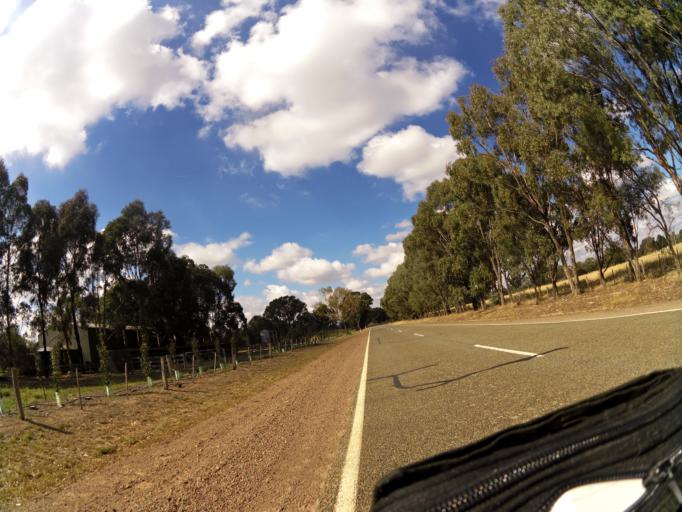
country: AU
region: Victoria
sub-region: Benalla
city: Benalla
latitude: -36.5909
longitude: 146.0095
